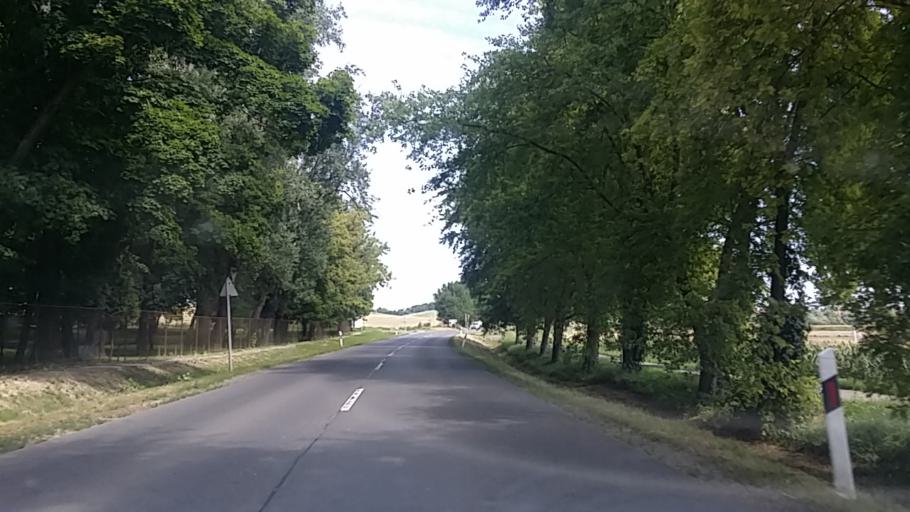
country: HU
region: Baranya
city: Sasd
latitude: 46.2926
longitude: 18.1219
